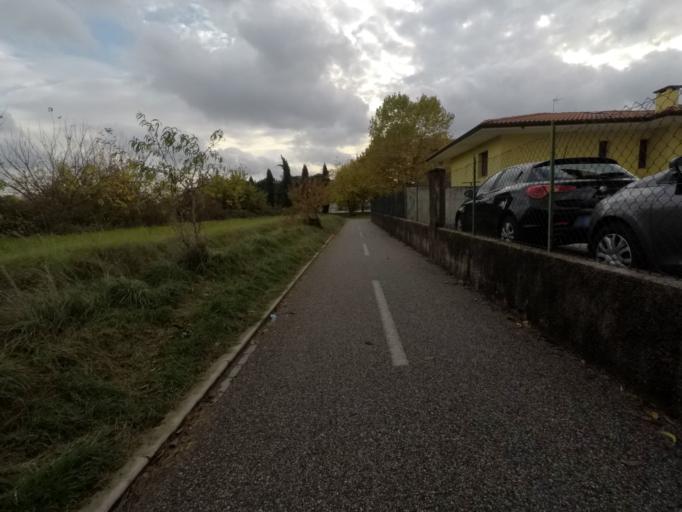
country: IT
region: Friuli Venezia Giulia
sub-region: Provincia di Udine
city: Colugna
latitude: 46.0814
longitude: 13.2051
